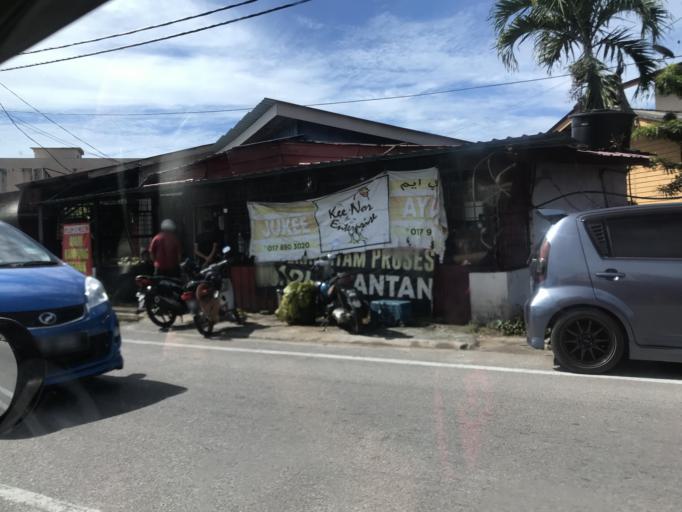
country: MY
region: Kelantan
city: Kota Bharu
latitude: 6.1200
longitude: 102.2003
